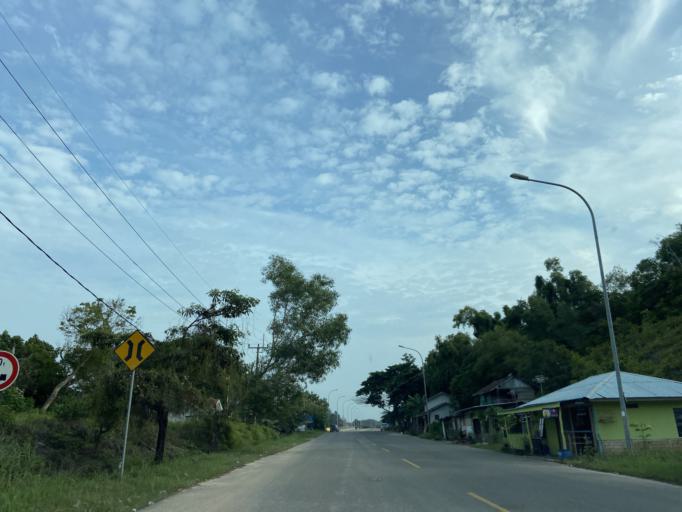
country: ID
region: Riau Islands
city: Tanjungpinang
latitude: 0.9433
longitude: 104.0795
